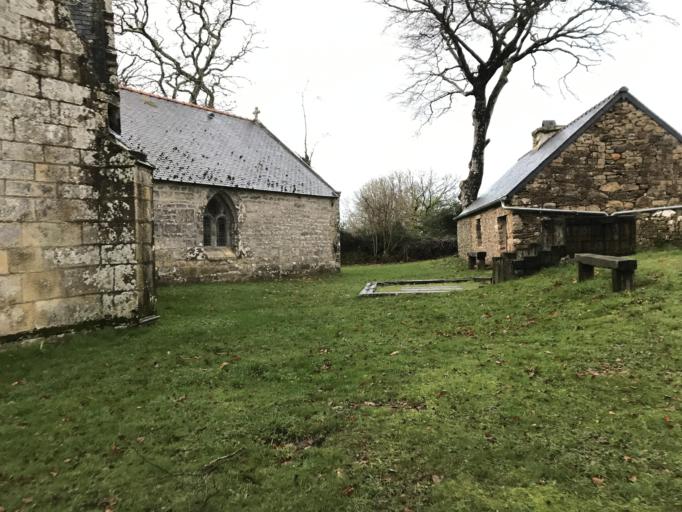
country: FR
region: Brittany
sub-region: Departement du Finistere
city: Loperhet
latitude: 48.3615
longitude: -4.3292
